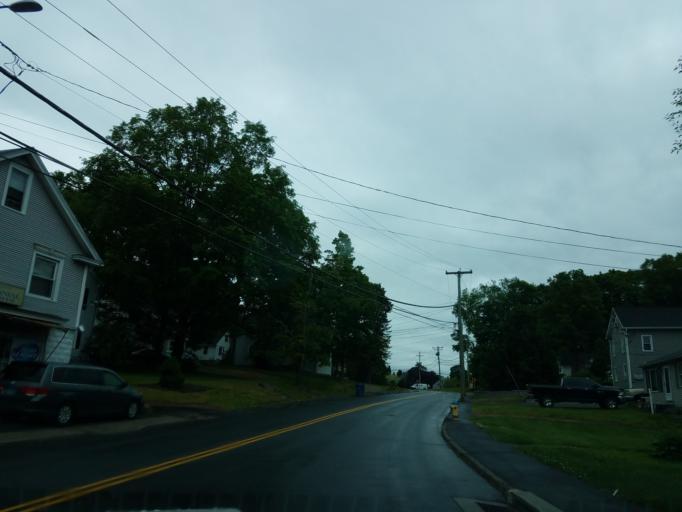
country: US
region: Connecticut
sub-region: Hartford County
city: Plainville
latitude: 41.5974
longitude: -72.8701
